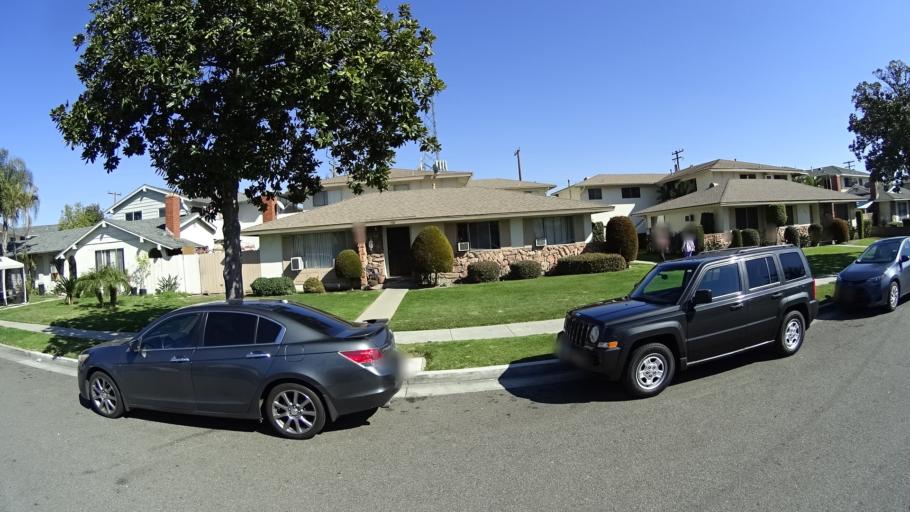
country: US
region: California
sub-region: Orange County
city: Anaheim
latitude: 33.8357
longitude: -117.9492
